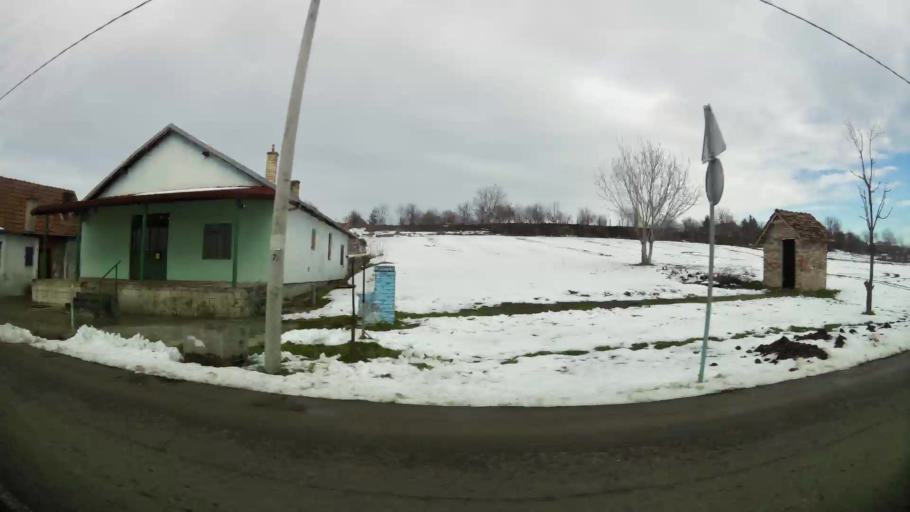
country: RS
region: Central Serbia
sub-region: Belgrade
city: Surcin
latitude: 44.7892
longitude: 20.2826
